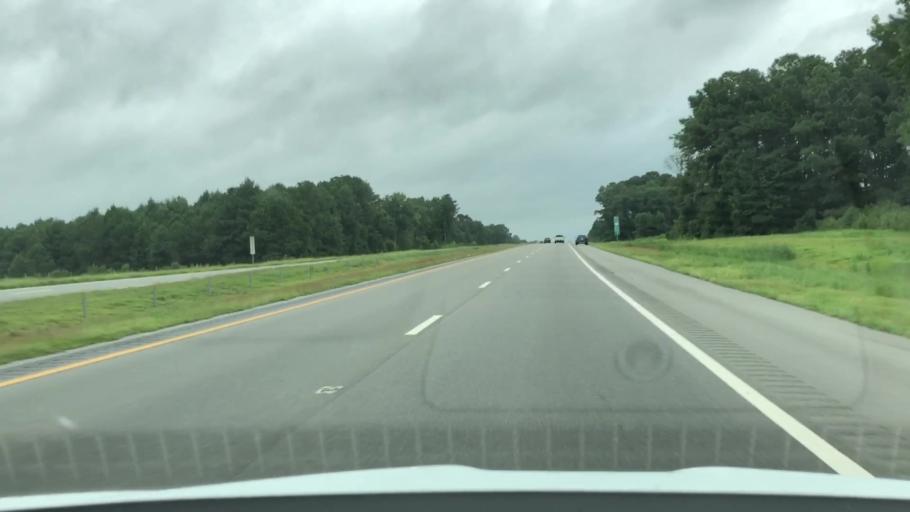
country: US
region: North Carolina
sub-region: Lenoir County
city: La Grange
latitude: 35.3334
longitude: -77.8429
